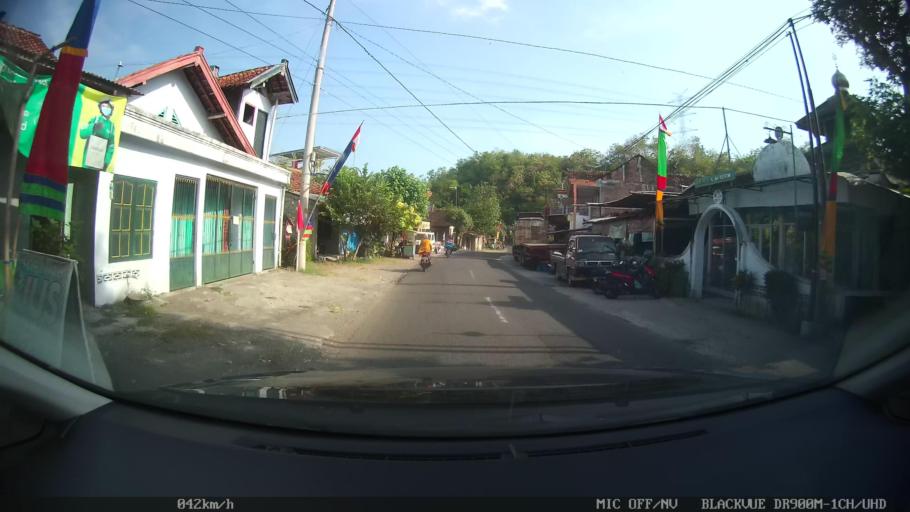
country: ID
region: Daerah Istimewa Yogyakarta
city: Bantul
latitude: -7.8738
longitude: 110.3153
